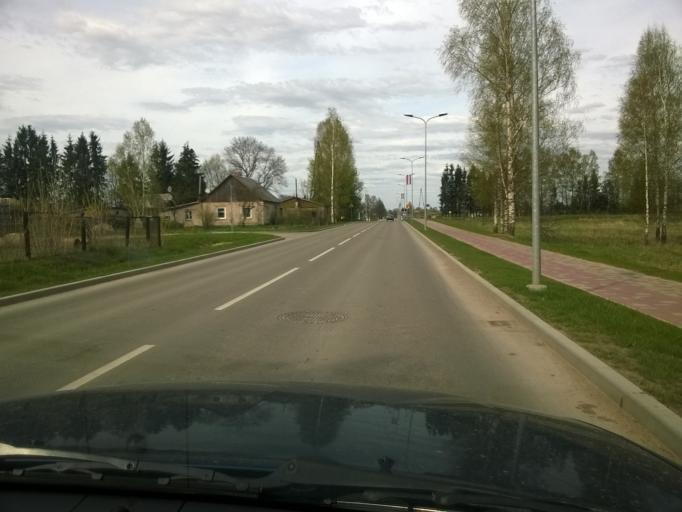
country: LV
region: Vilanu
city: Vilani
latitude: 56.5604
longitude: 26.9263
